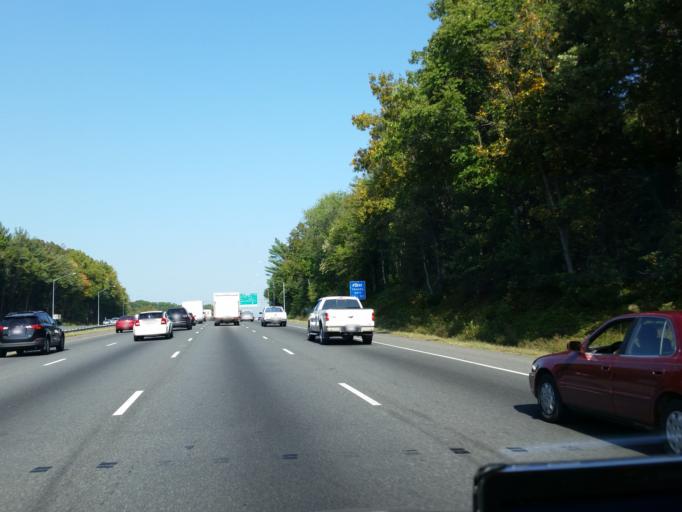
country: US
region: Maryland
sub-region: Prince George's County
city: New Carrollton
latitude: 38.9870
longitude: -76.8815
